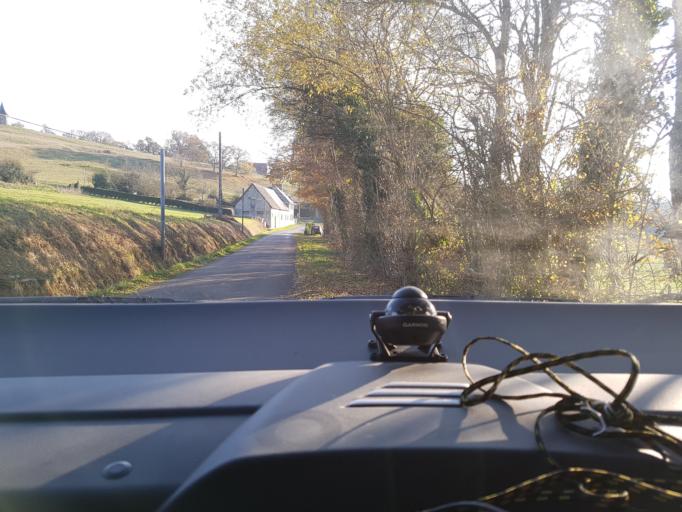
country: FR
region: Lower Normandy
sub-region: Departement du Calvados
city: Conde-sur-Noireau
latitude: 48.8825
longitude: -0.5853
